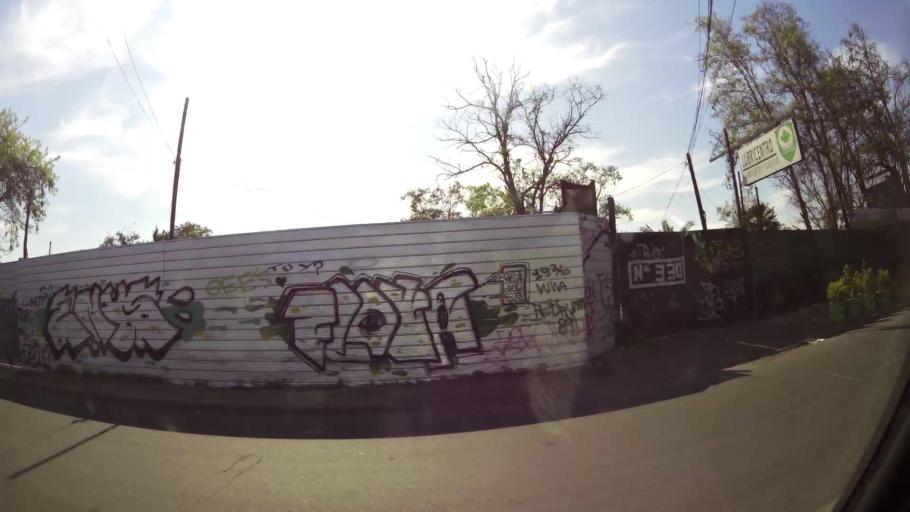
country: CL
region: Santiago Metropolitan
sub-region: Provincia de Santiago
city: Lo Prado
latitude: -33.4805
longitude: -70.7398
